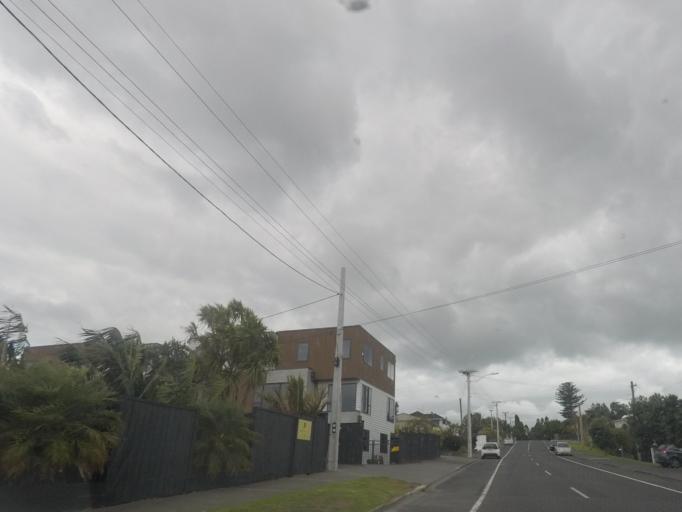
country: NZ
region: Auckland
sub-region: Auckland
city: Tamaki
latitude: -36.8697
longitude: 174.8791
